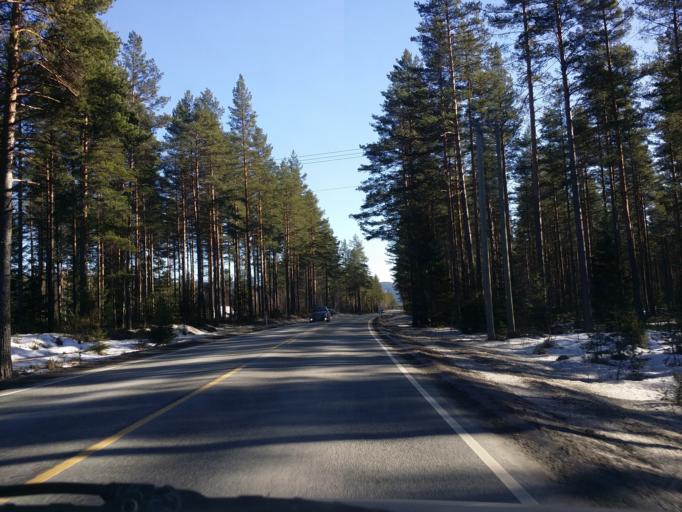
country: NO
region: Buskerud
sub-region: Ringerike
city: Honefoss
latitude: 60.3156
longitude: 10.1489
